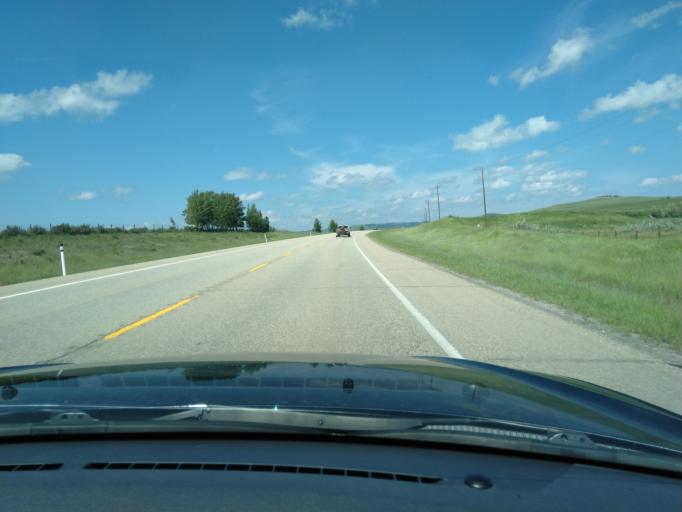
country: CA
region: Alberta
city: Cochrane
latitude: 51.2090
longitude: -114.5215
